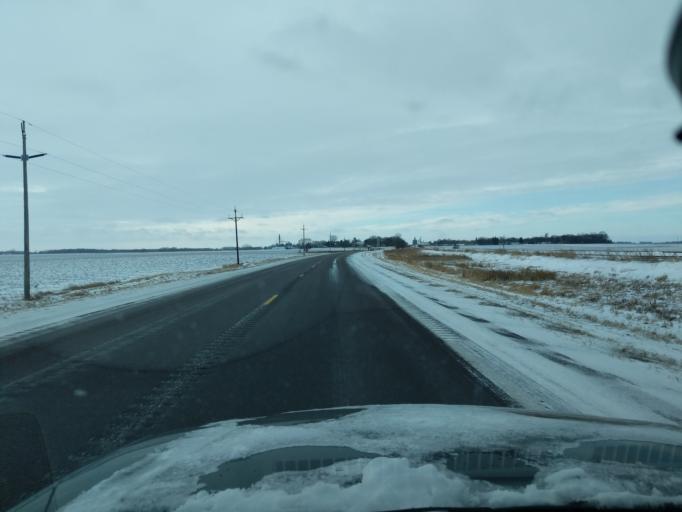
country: US
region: Minnesota
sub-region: McLeod County
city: Hutchinson
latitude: 44.7220
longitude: -94.4629
